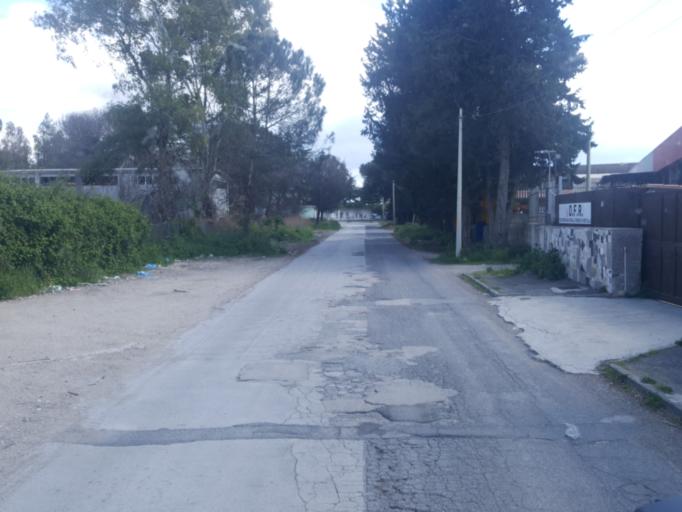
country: IT
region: Campania
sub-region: Provincia di Napoli
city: Torretta-Scalzapecora
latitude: 40.9337
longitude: 14.1056
